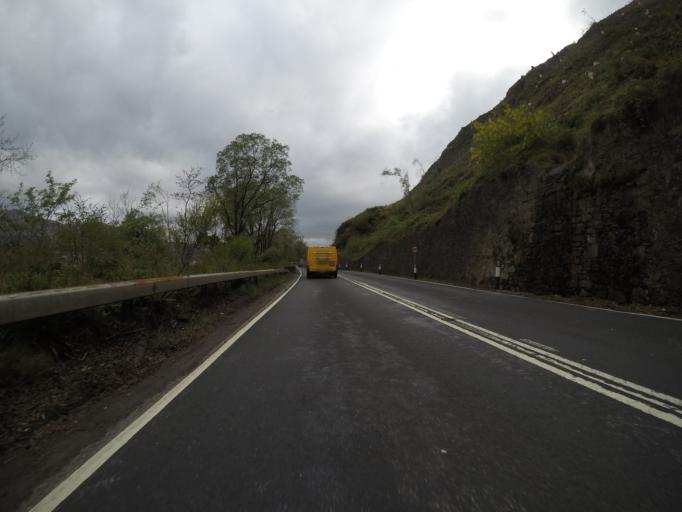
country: GB
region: Scotland
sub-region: Highland
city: Fort William
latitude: 56.7362
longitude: -5.2162
